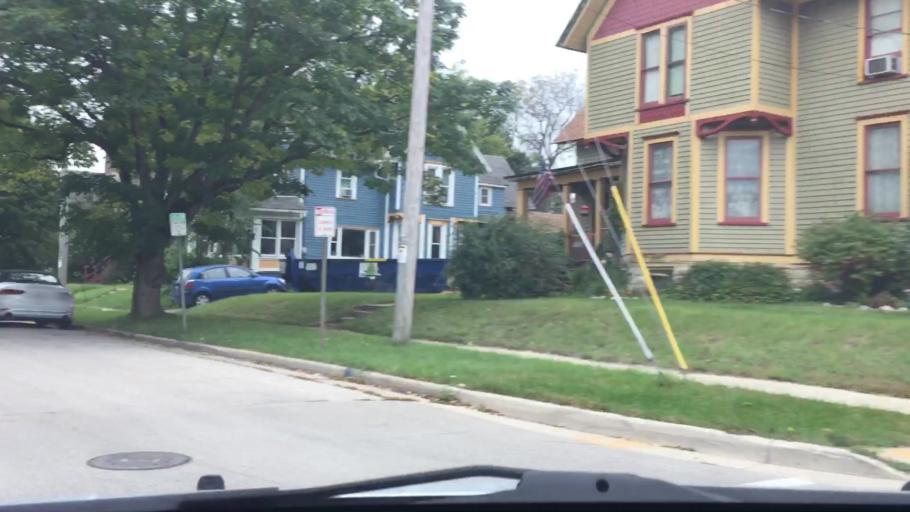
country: US
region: Wisconsin
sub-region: Waukesha County
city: Waukesha
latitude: 43.0119
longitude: -88.2254
